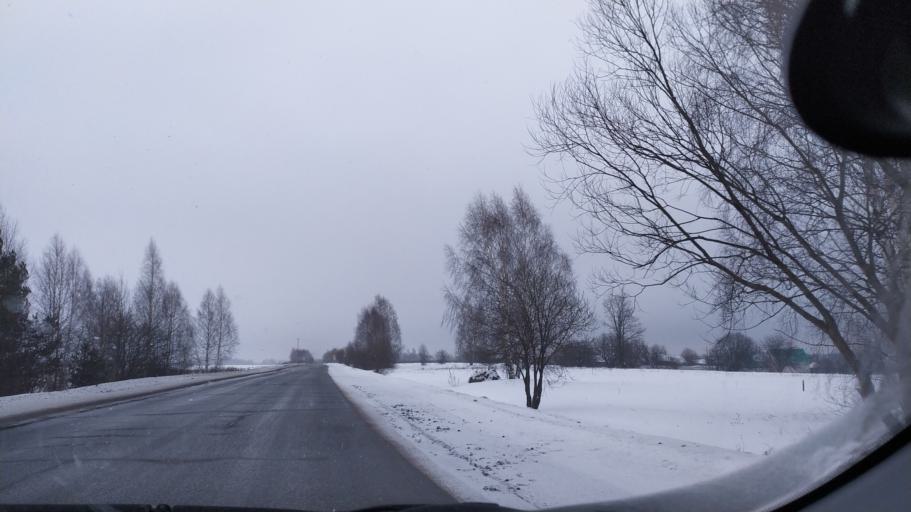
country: RU
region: Mariy-El
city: Krasnogorskiy
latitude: 56.1497
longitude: 48.1411
